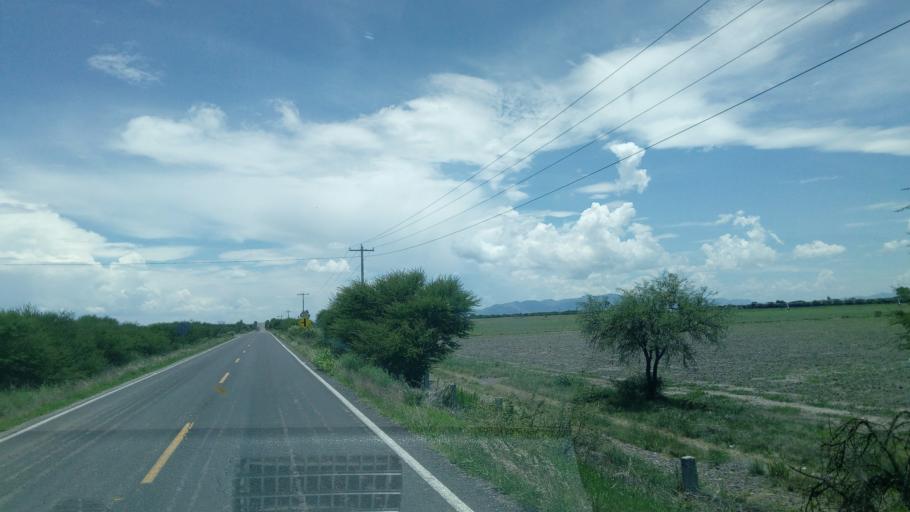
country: MX
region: Durango
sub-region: Durango
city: Jose Refugio Salcido
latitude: 24.1591
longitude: -104.5198
